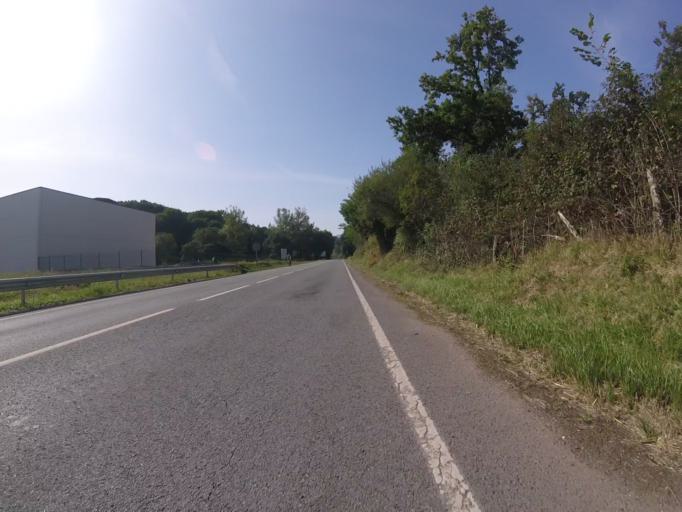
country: ES
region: Navarre
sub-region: Provincia de Navarra
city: Zugarramurdi
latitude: 43.1783
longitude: -1.4917
